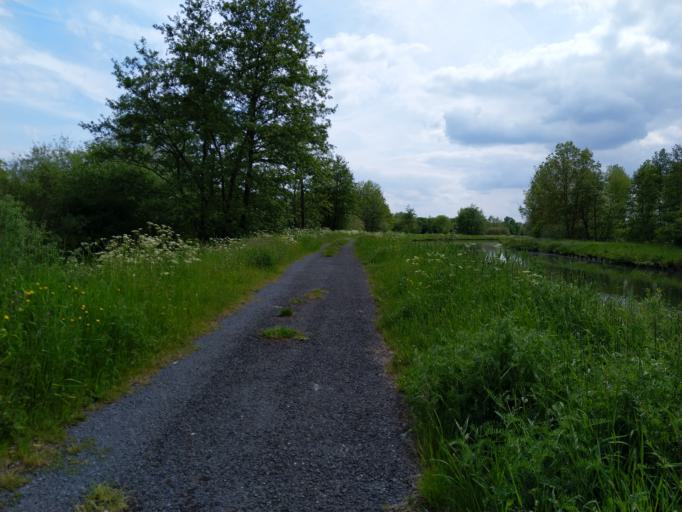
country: FR
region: Picardie
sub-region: Departement de l'Aisne
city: Wassigny
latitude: 50.0638
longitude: 3.6490
